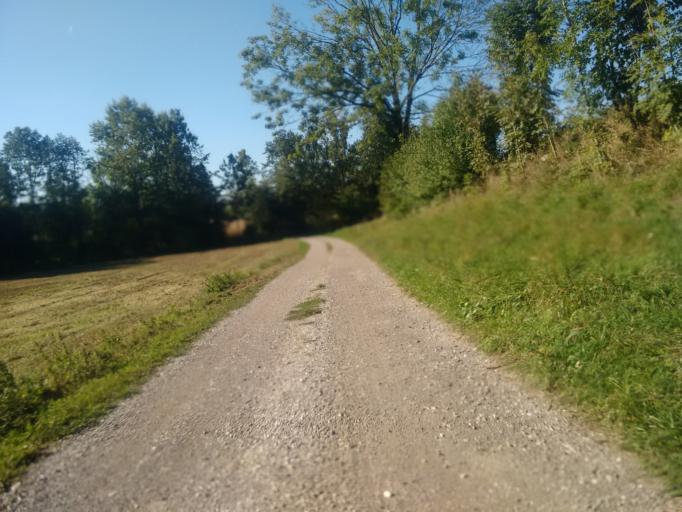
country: AT
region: Upper Austria
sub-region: Wels-Land
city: Buchkirchen
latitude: 48.1973
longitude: 13.9802
